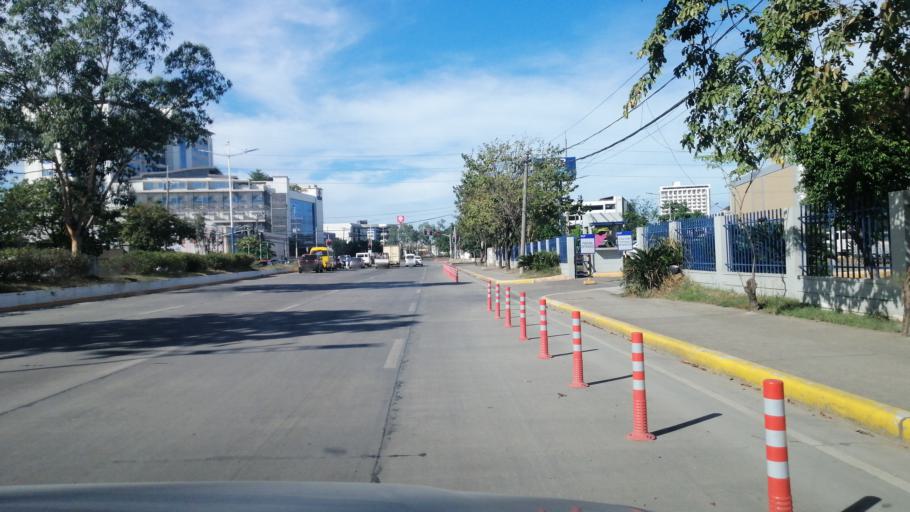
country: PH
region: Central Visayas
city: Mandaue City
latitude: 10.3184
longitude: 123.9302
